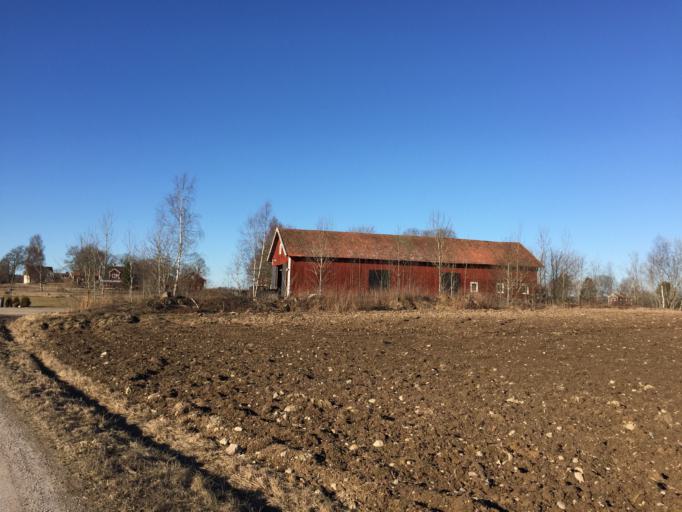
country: SE
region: Soedermanland
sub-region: Vingakers Kommun
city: Vingaker
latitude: 59.0471
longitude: 15.8129
